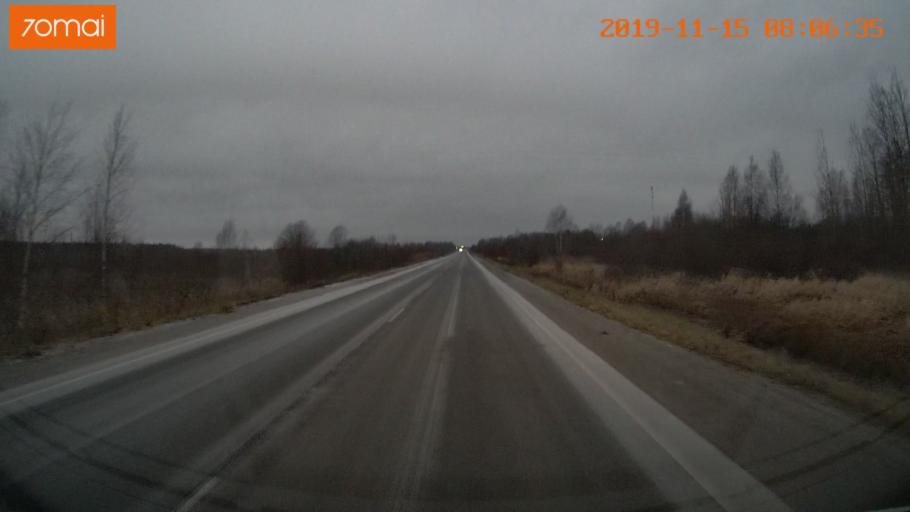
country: RU
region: Vologda
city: Cherepovets
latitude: 59.0229
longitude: 38.0349
